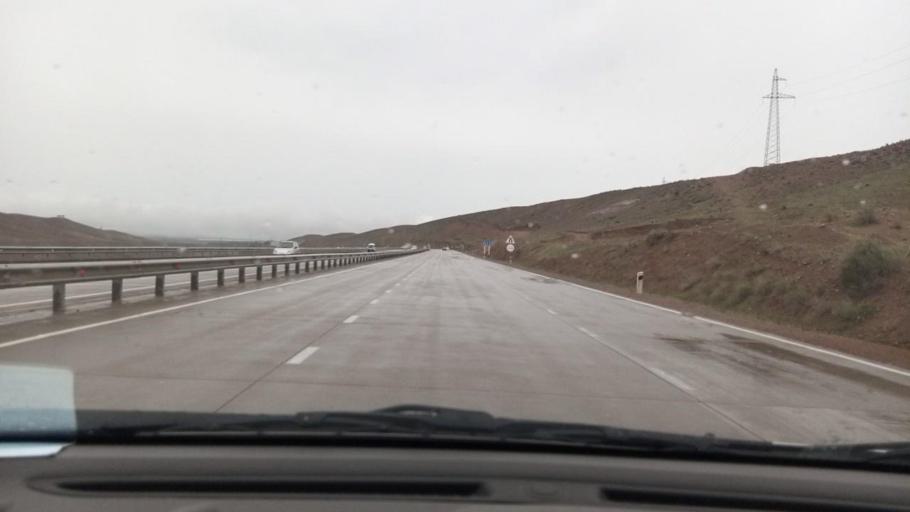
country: UZ
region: Namangan
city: Pop Shahri
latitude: 40.9332
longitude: 70.6997
